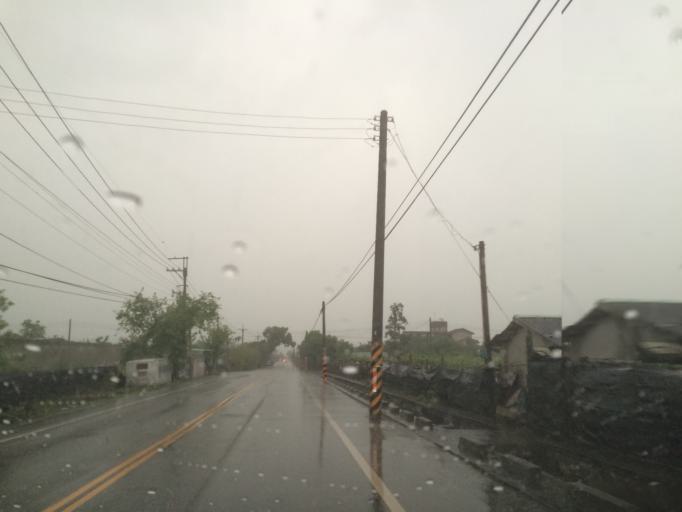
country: TW
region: Taiwan
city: Fengyuan
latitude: 24.2139
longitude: 120.8032
